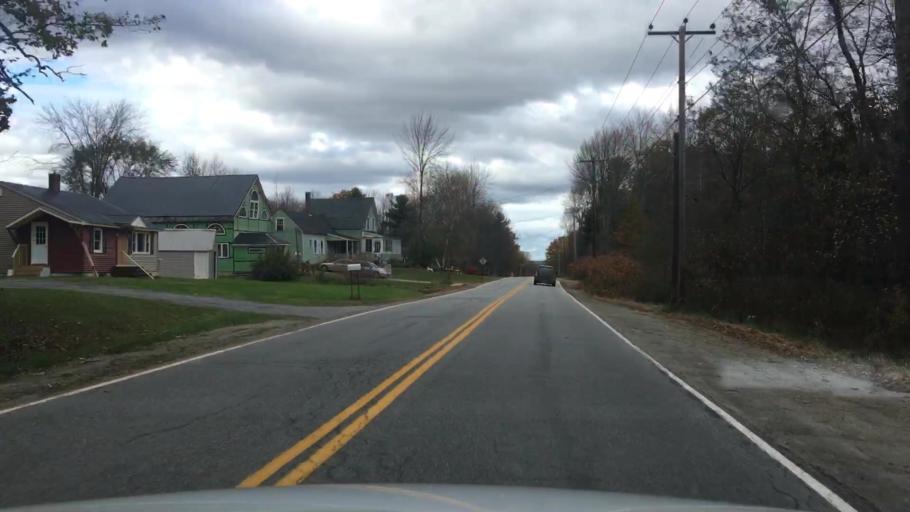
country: US
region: Maine
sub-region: Kennebec County
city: Monmouth
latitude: 44.1842
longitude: -70.0656
